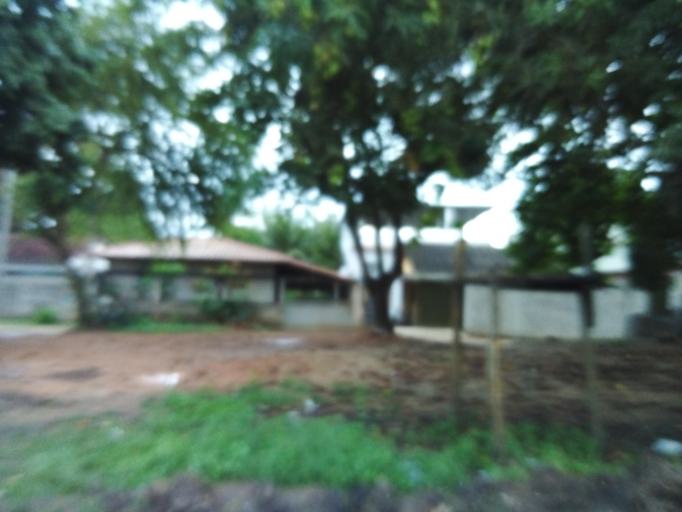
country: BR
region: Espirito Santo
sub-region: Marilandia
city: Marilandia
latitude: -19.5334
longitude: -40.4883
